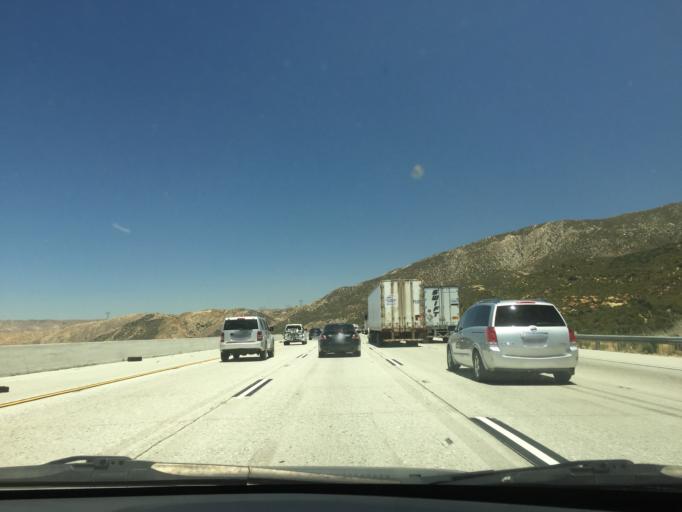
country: US
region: California
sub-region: San Bernardino County
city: Oak Hills
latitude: 34.2818
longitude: -117.4521
